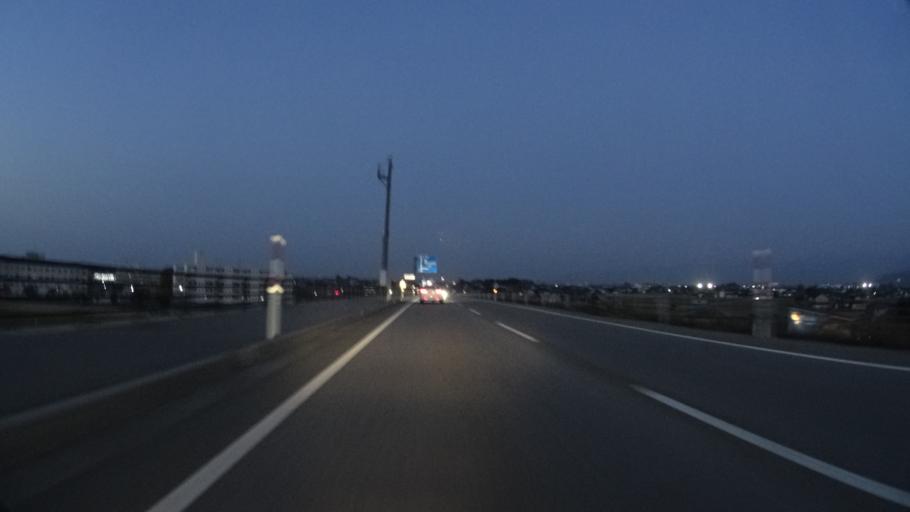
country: JP
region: Toyama
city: Uozu
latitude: 36.8801
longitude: 137.4320
